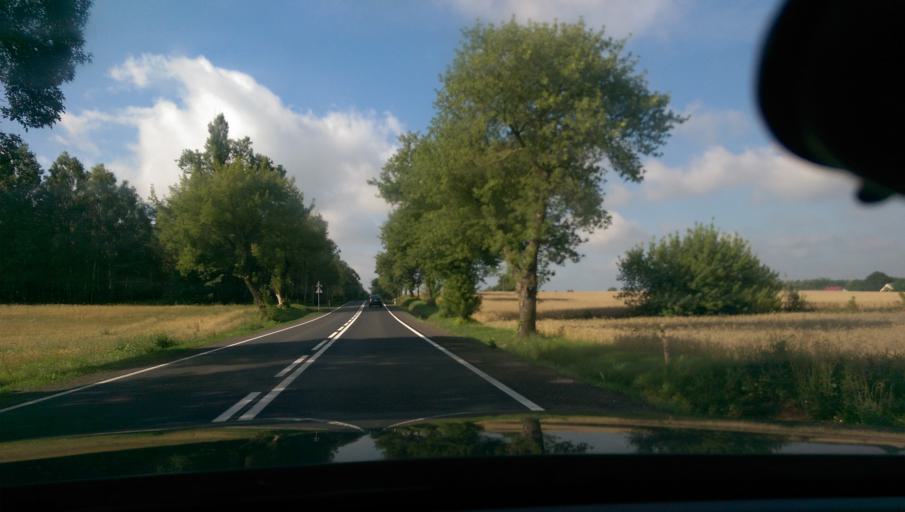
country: PL
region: Masovian Voivodeship
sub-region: Powiat ciechanowski
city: Ojrzen
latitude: 52.7443
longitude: 20.5266
